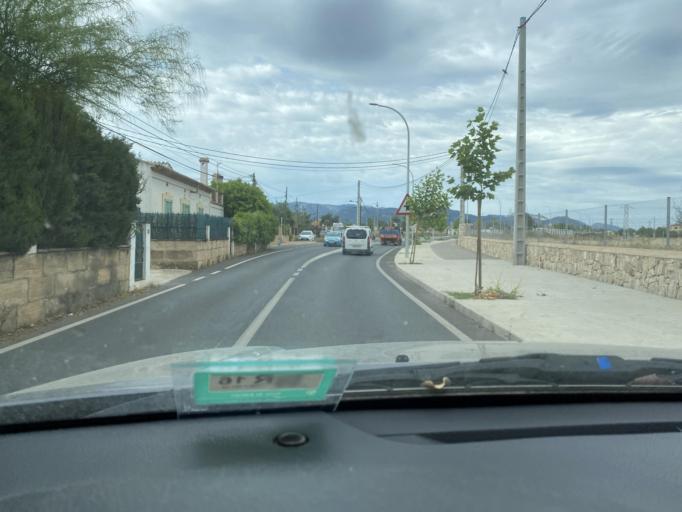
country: ES
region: Balearic Islands
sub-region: Illes Balears
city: Palma
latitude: 39.6116
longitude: 2.6809
